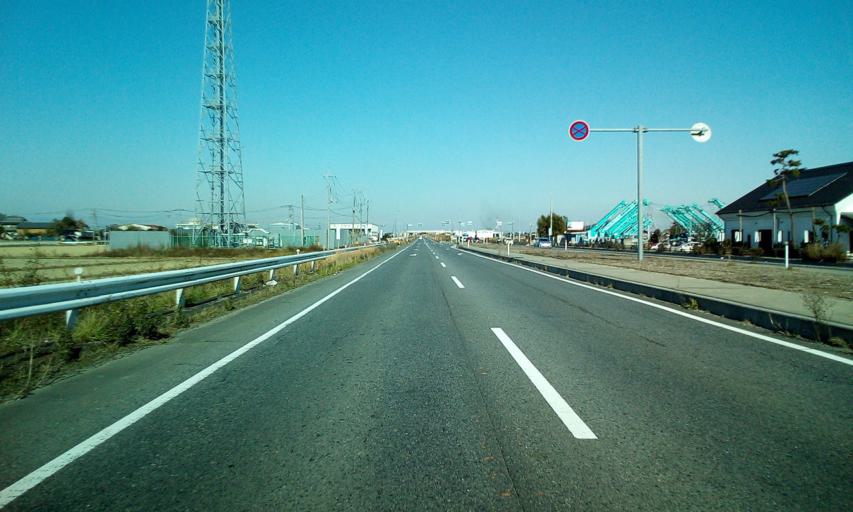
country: JP
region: Saitama
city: Satte
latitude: 36.0604
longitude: 139.7726
